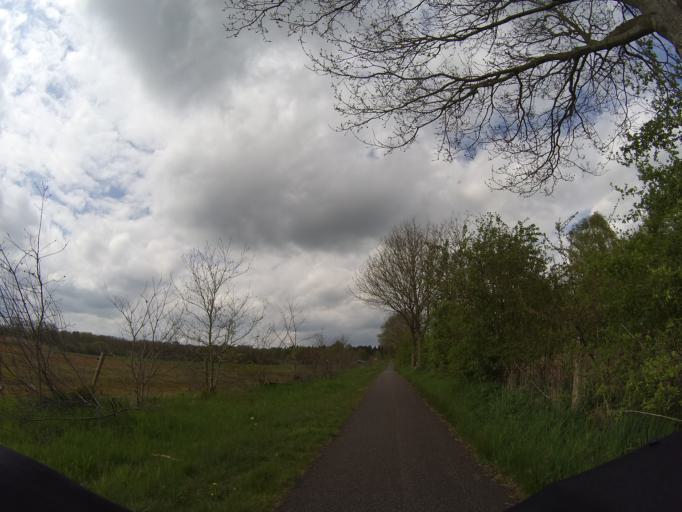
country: NL
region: Overijssel
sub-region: Gemeente Hardenberg
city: Hardenberg
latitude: 52.5325
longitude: 6.5685
